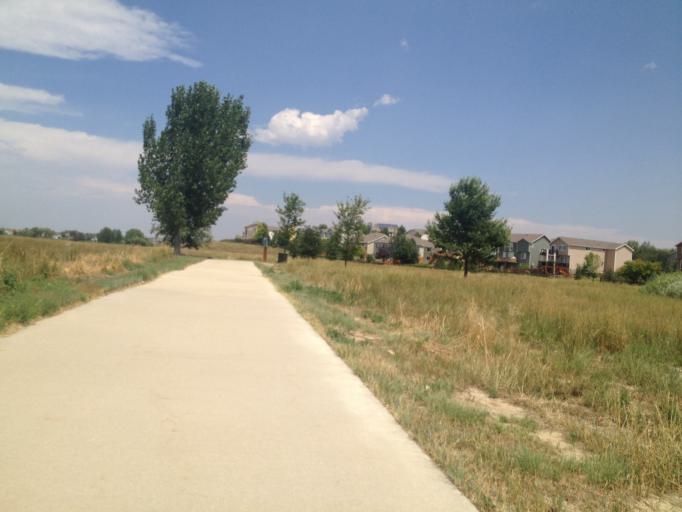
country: US
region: Colorado
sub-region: Boulder County
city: Erie
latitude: 40.0216
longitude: -105.0449
